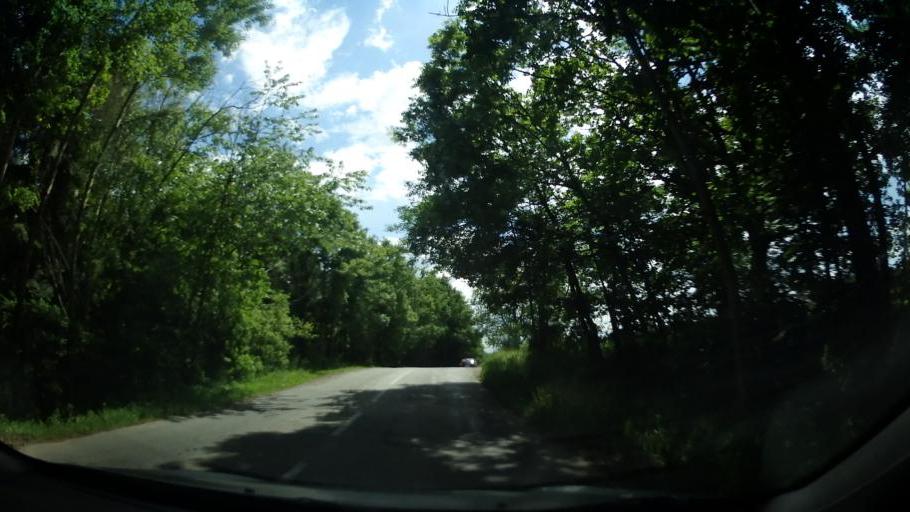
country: CZ
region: South Moravian
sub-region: Okres Blansko
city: Letovice
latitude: 49.5808
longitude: 16.5860
